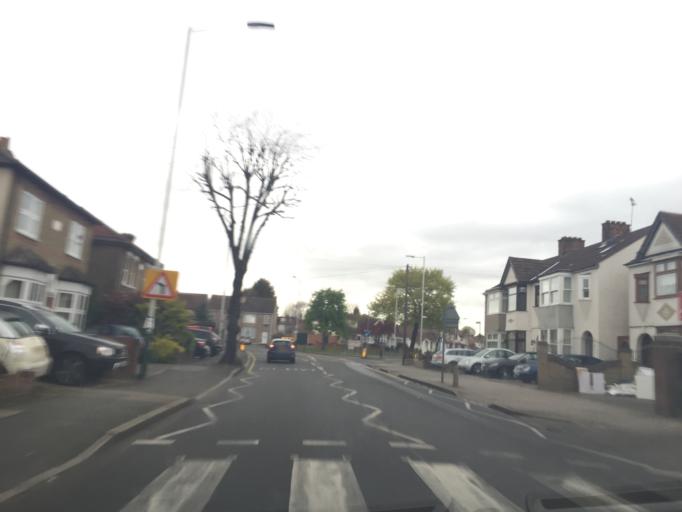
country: GB
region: England
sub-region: Greater London
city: Collier Row
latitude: 51.5883
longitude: 0.1718
